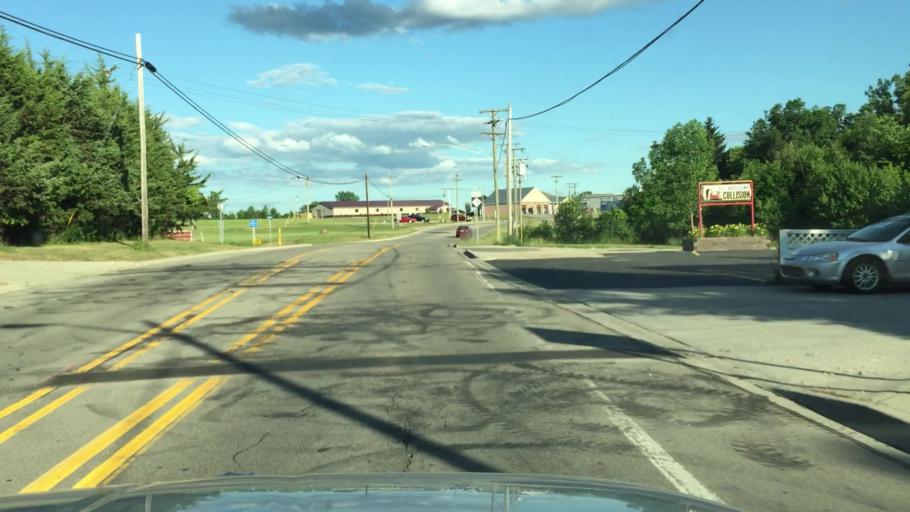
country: US
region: Michigan
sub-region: Saint Clair County
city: Yale
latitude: 43.1233
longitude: -82.7936
